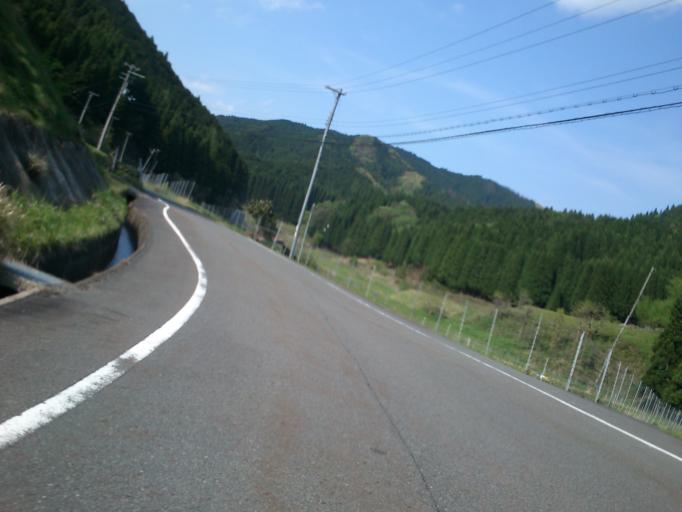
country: JP
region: Kyoto
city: Fukuchiyama
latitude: 35.3665
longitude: 135.0107
